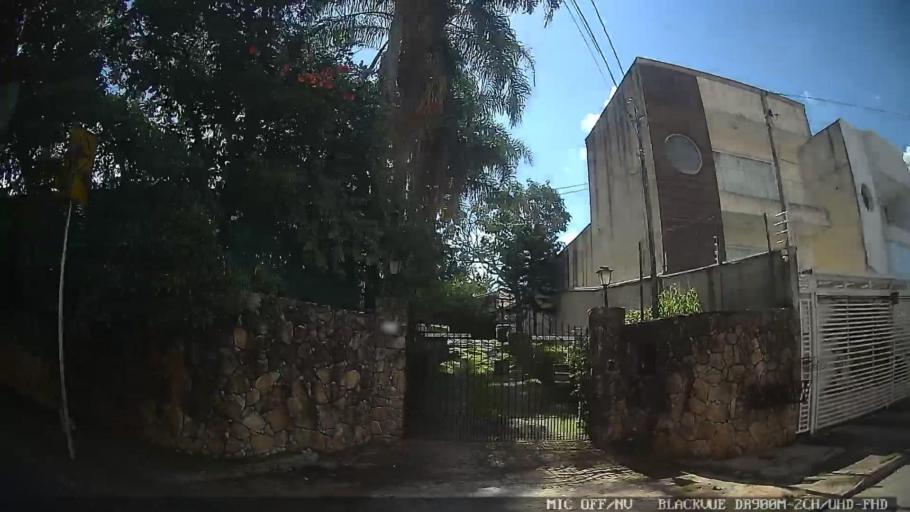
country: BR
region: Sao Paulo
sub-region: Atibaia
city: Atibaia
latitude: -23.1453
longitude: -46.5607
